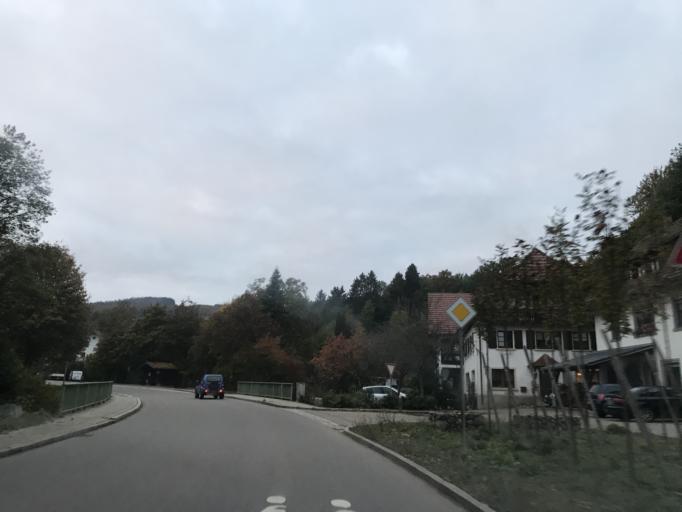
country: DE
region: Baden-Wuerttemberg
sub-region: Freiburg Region
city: Rickenbach
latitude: 47.6247
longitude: 8.0053
